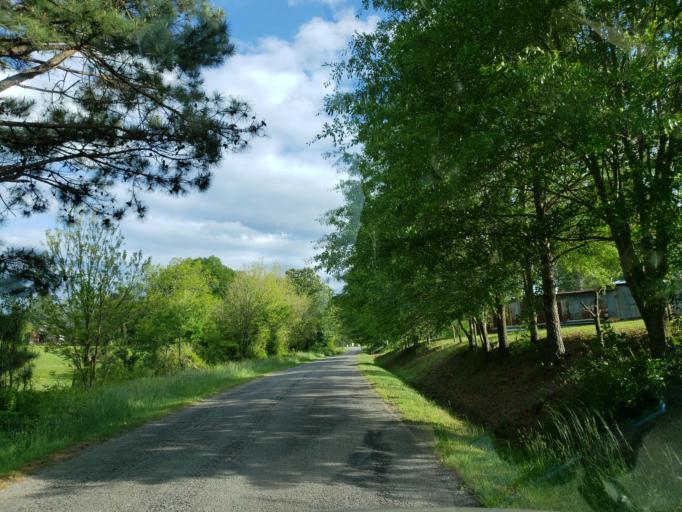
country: US
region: Georgia
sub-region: Haralson County
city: Tallapoosa
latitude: 33.8145
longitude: -85.2907
